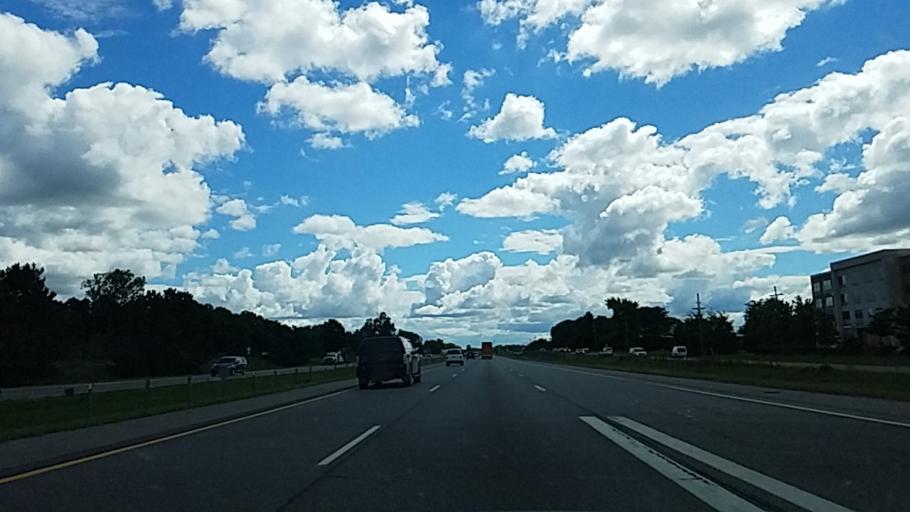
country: US
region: Michigan
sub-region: Livingston County
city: Brighton
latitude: 42.5028
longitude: -83.7581
